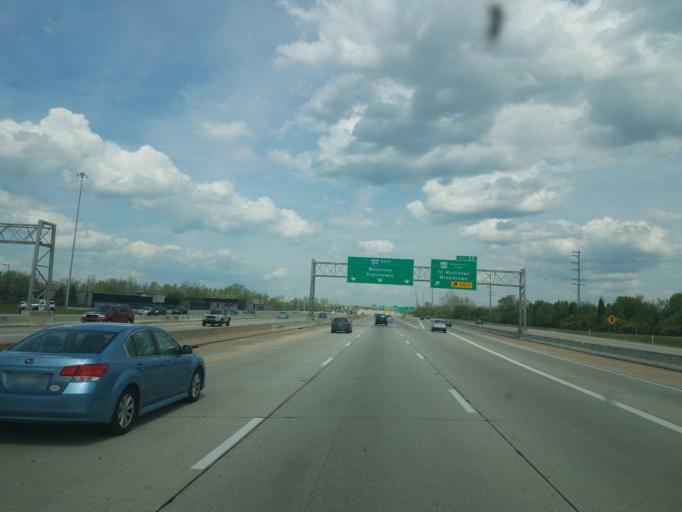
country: US
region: Kentucky
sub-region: Jefferson County
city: Saint Regis Park
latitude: 38.2389
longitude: -85.6217
